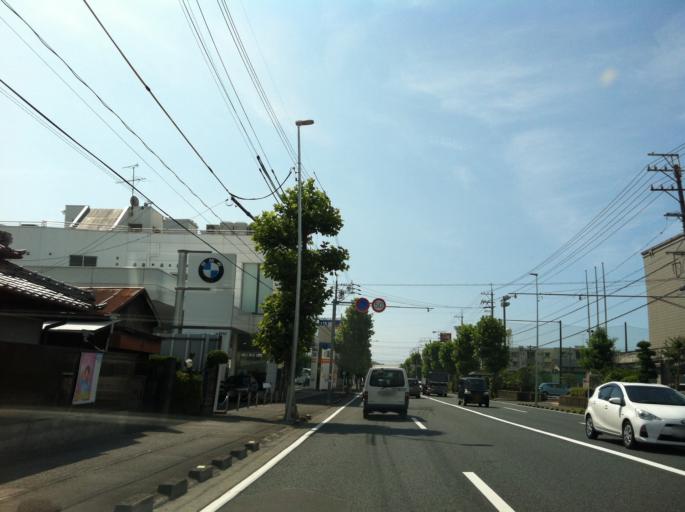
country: JP
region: Shizuoka
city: Shizuoka-shi
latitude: 34.9525
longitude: 138.3852
